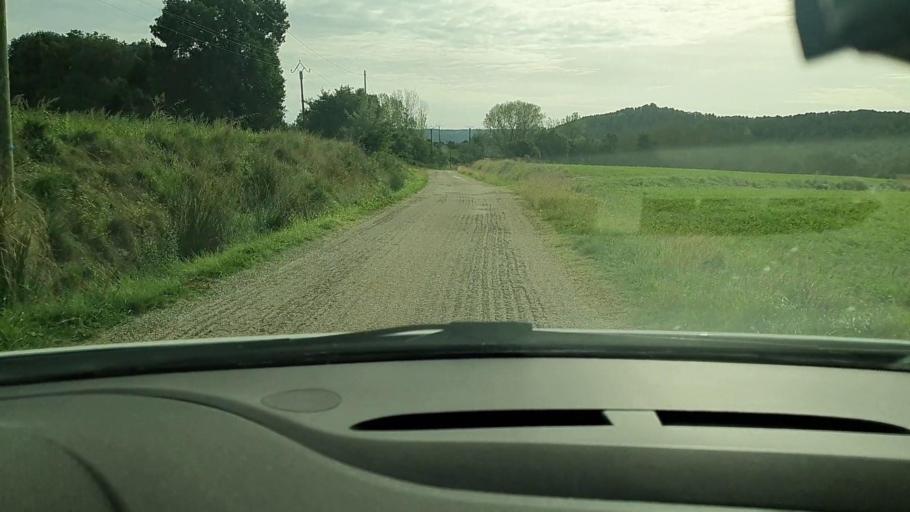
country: FR
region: Languedoc-Roussillon
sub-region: Departement du Gard
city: Montaren-et-Saint-Mediers
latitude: 44.0901
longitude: 4.3428
